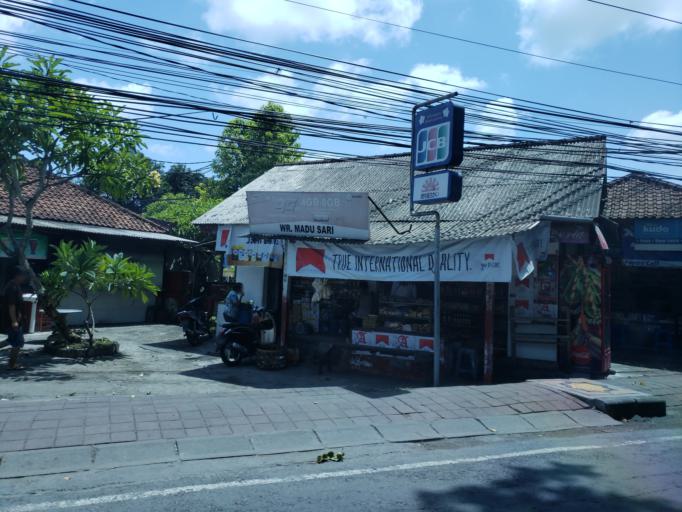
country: ID
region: Bali
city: Jimbaran
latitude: -8.7782
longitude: 115.1693
